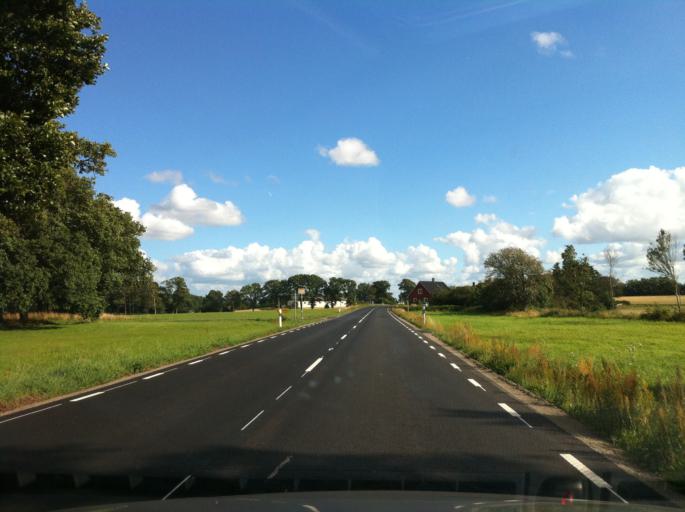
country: SE
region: Skane
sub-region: Bastads Kommun
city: Forslov
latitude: 56.3913
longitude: 12.8059
